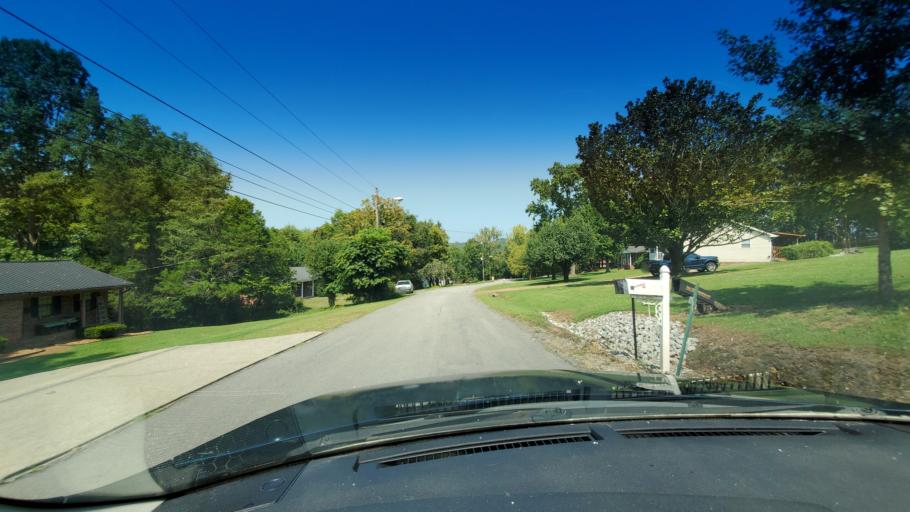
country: US
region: Tennessee
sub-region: Smith County
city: Carthage
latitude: 36.2517
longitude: -85.9604
